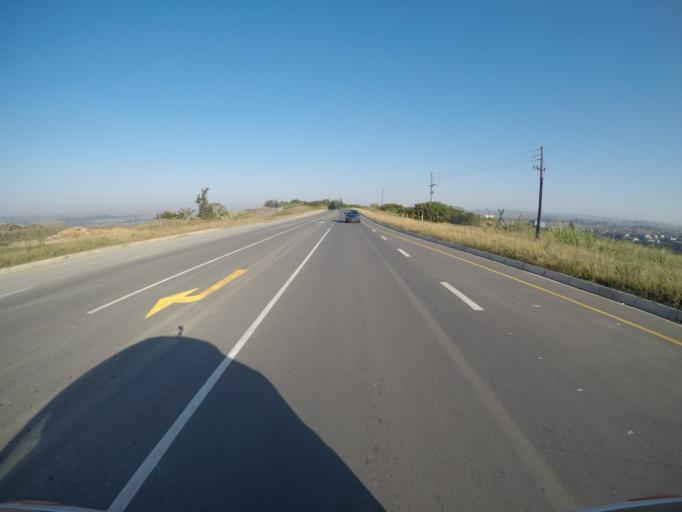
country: ZA
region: KwaZulu-Natal
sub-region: iLembe District Municipality
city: Stanger
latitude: -29.4261
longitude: 31.2621
